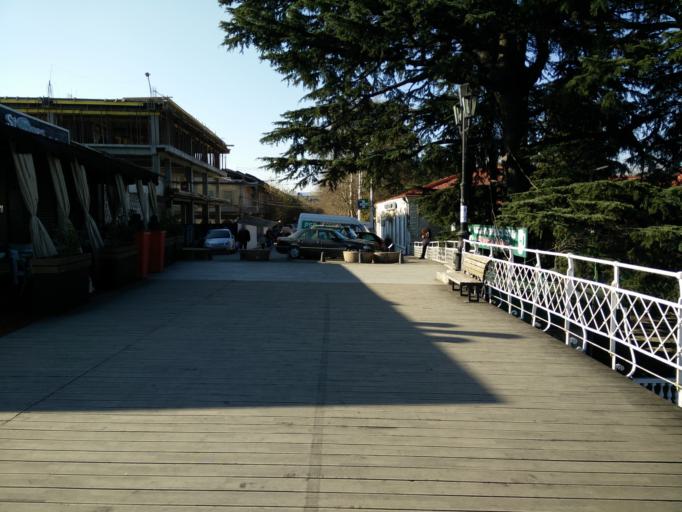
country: GE
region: Imereti
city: Kutaisi
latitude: 42.2686
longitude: 42.7001
